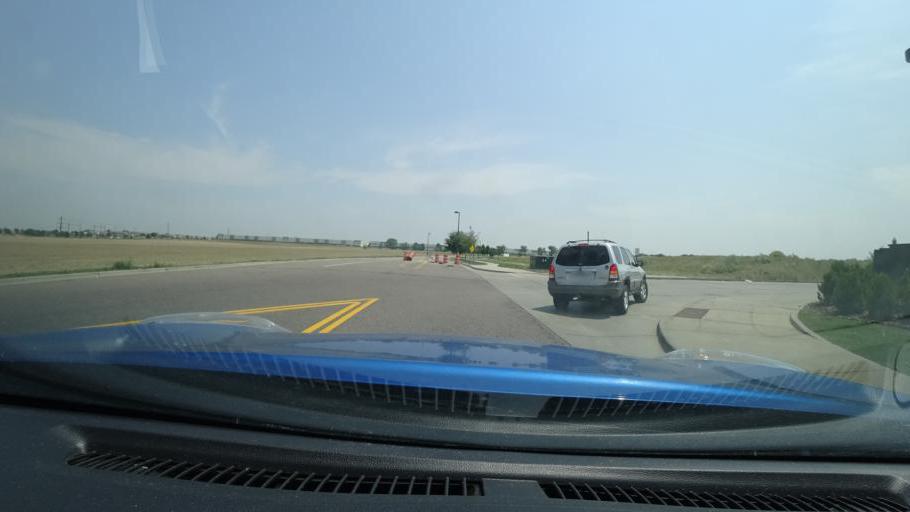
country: US
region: Colorado
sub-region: Adams County
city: Aurora
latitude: 39.7645
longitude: -104.7712
